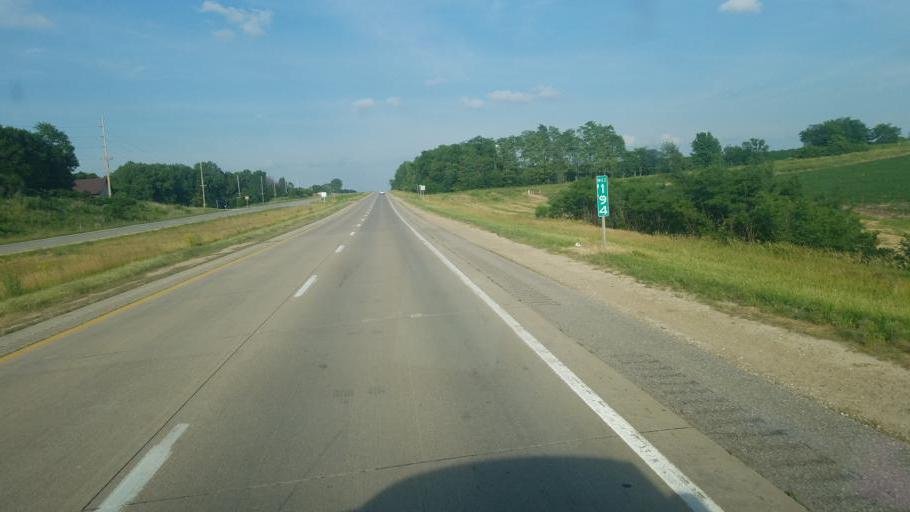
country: US
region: Iowa
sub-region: Marshall County
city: Marshalltown
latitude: 42.0061
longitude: -92.7485
